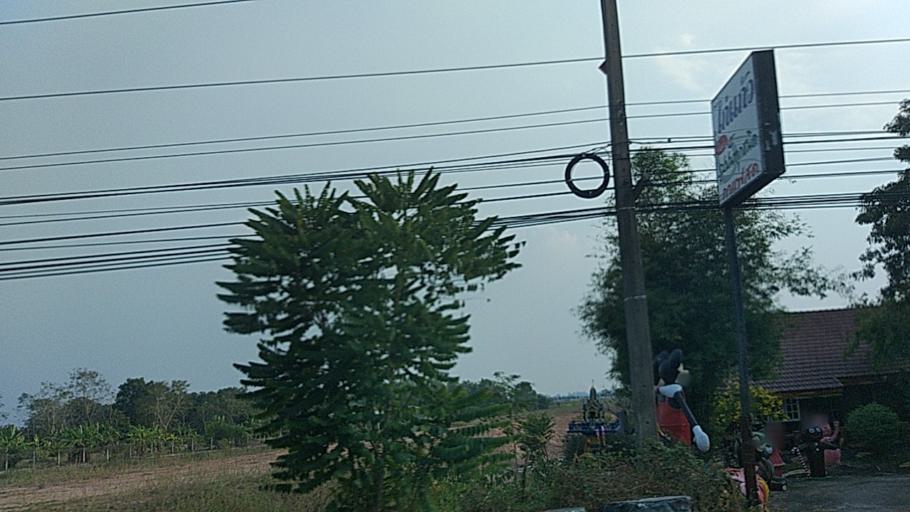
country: TH
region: Nakhon Nayok
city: Nakhon Nayok
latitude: 14.2217
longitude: 101.1391
